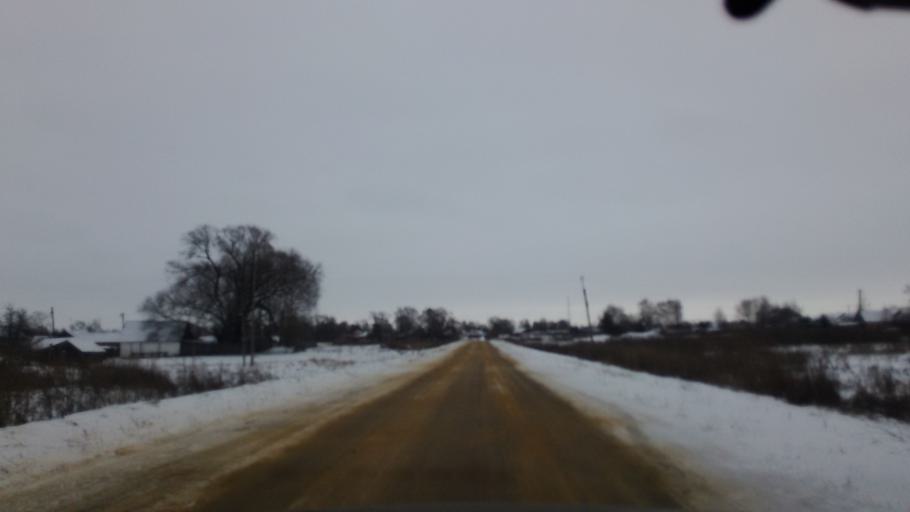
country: RU
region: Tula
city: Bogoroditsk
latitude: 53.7664
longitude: 37.9782
